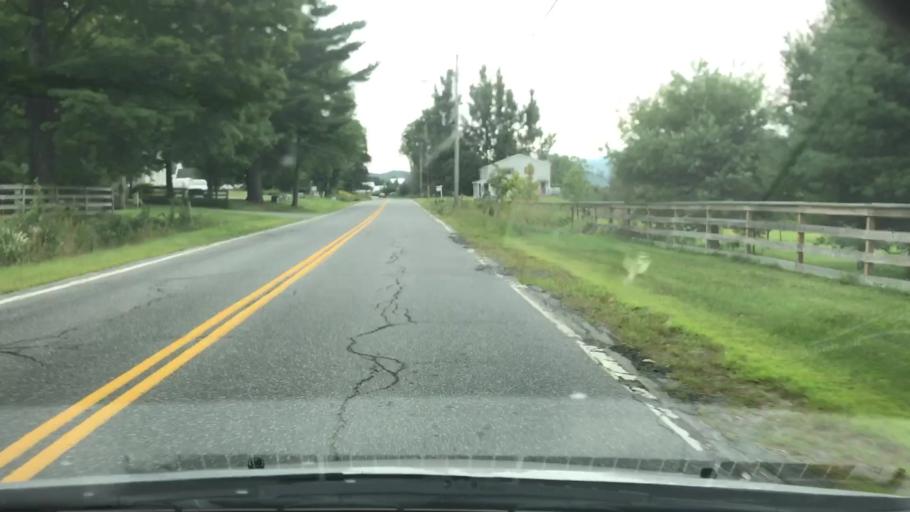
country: US
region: New Hampshire
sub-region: Grafton County
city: Haverhill
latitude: 44.0285
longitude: -72.0675
